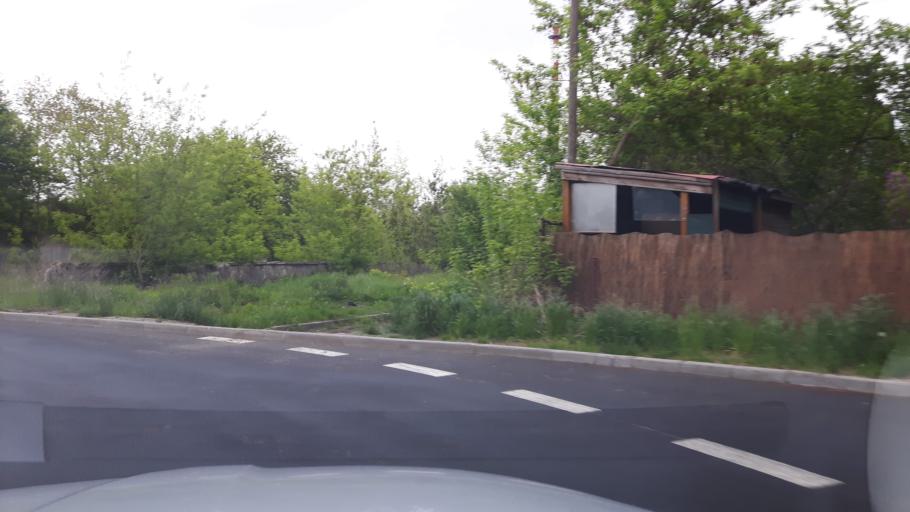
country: PL
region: Masovian Voivodeship
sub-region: Warszawa
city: Rembertow
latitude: 52.2687
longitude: 21.1798
